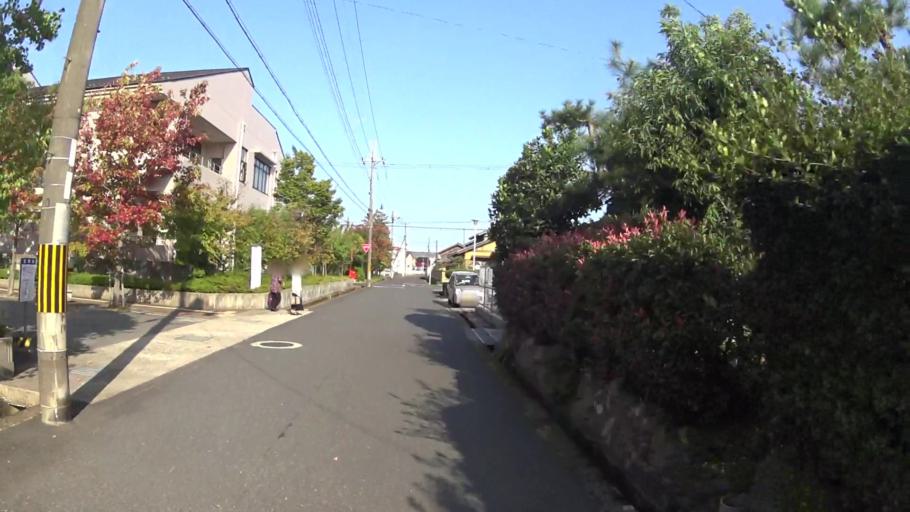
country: JP
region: Kyoto
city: Miyazu
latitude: 35.5635
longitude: 135.1507
